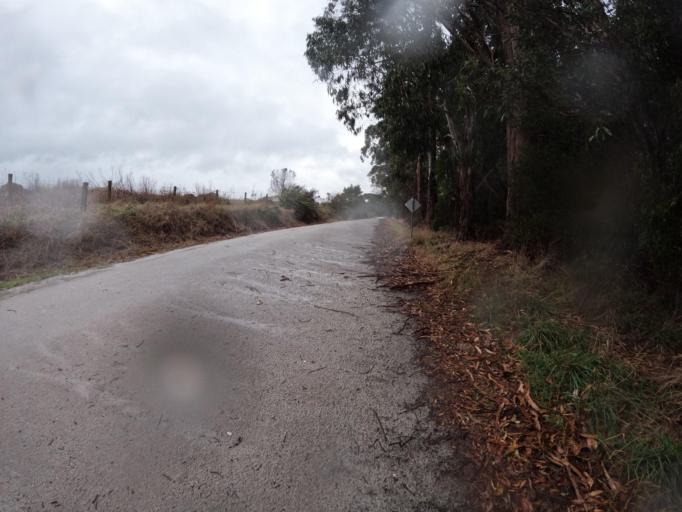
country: AU
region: Victoria
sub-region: Latrobe
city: Morwell
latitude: -38.6894
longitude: 146.1367
